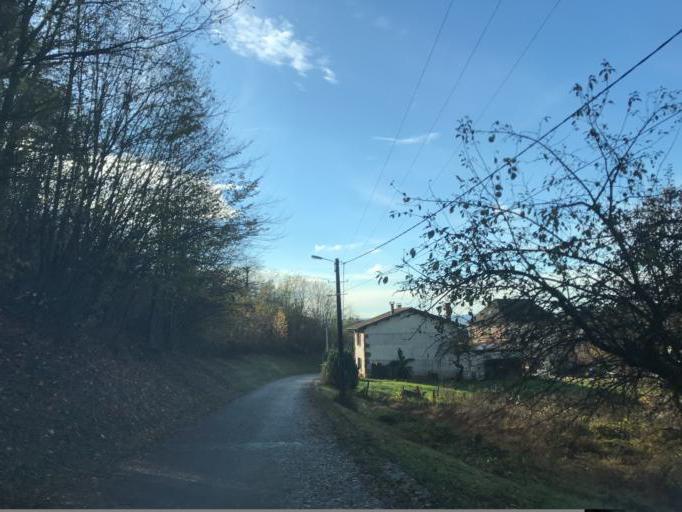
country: FR
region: Rhone-Alpes
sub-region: Departement de l'Ain
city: Jujurieux
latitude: 46.0427
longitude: 5.4130
